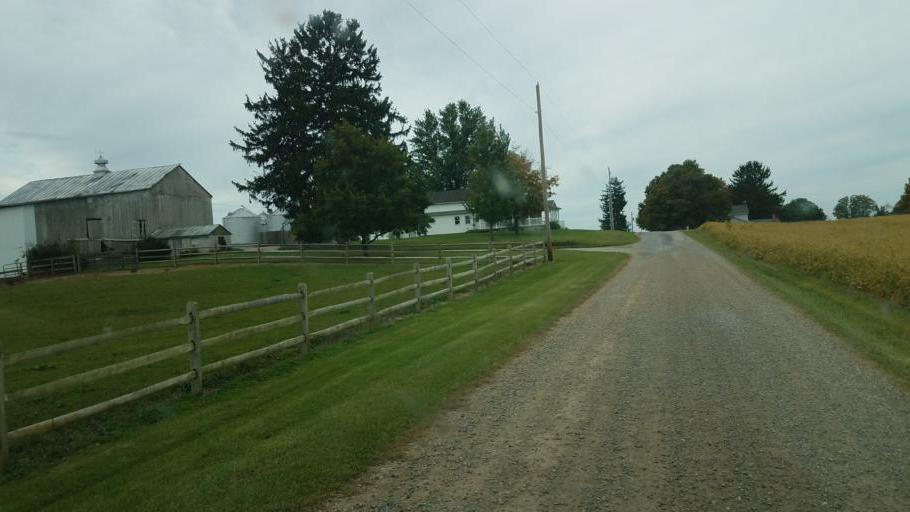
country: US
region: Ohio
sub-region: Knox County
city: Centerburg
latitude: 40.3387
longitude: -82.7034
